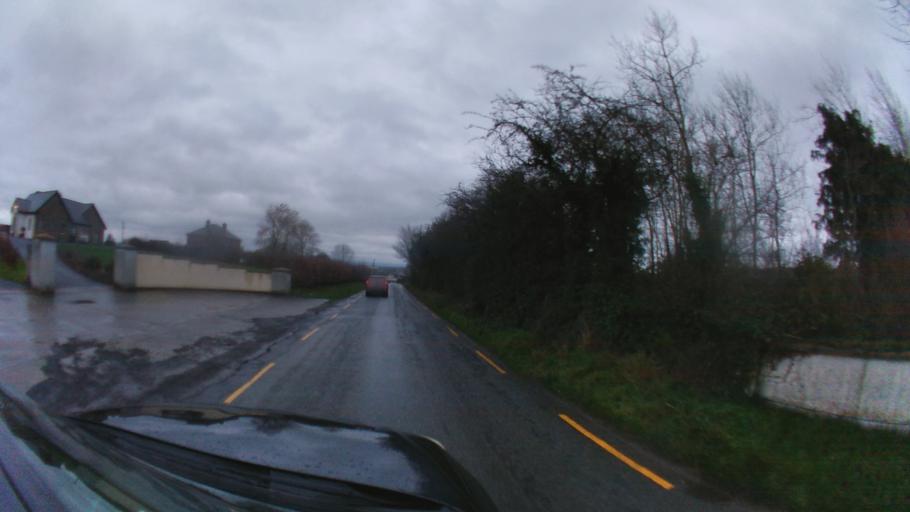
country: IE
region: Leinster
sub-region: County Carlow
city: Bagenalstown
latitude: 52.6203
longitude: -6.9911
